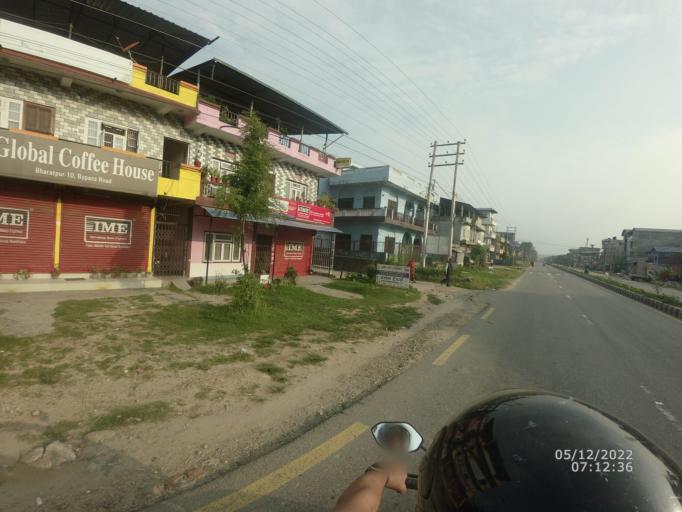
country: NP
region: Central Region
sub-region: Narayani Zone
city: Bharatpur
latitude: 27.6858
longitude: 84.4398
